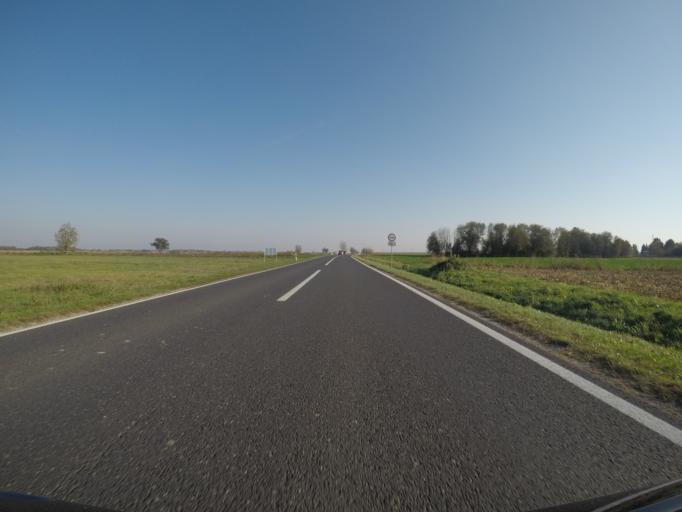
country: HR
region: Koprivnicko-Krizevacka
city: Kalinovac
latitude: 46.0230
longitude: 17.0801
